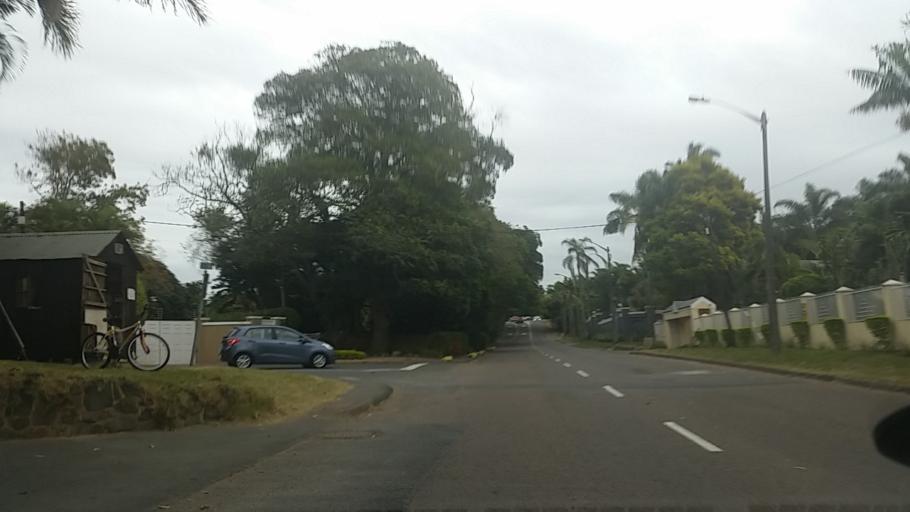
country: ZA
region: KwaZulu-Natal
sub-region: eThekwini Metropolitan Municipality
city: Berea
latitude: -29.8342
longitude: 30.9250
